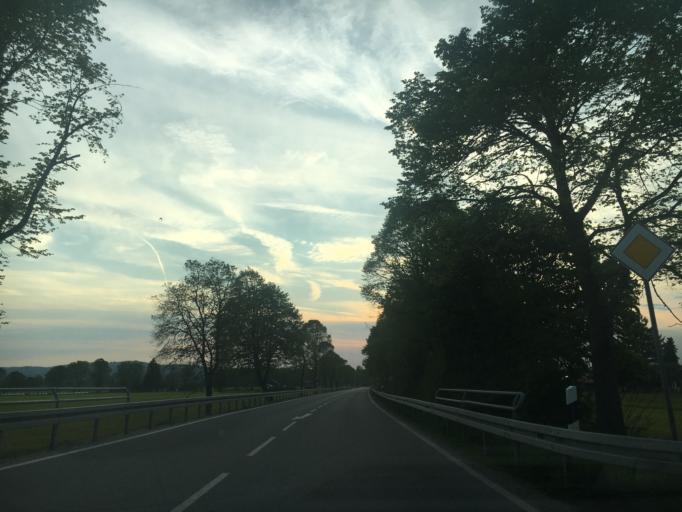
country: DE
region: Bavaria
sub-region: Upper Bavaria
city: Bichl
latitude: 47.7167
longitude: 11.4101
